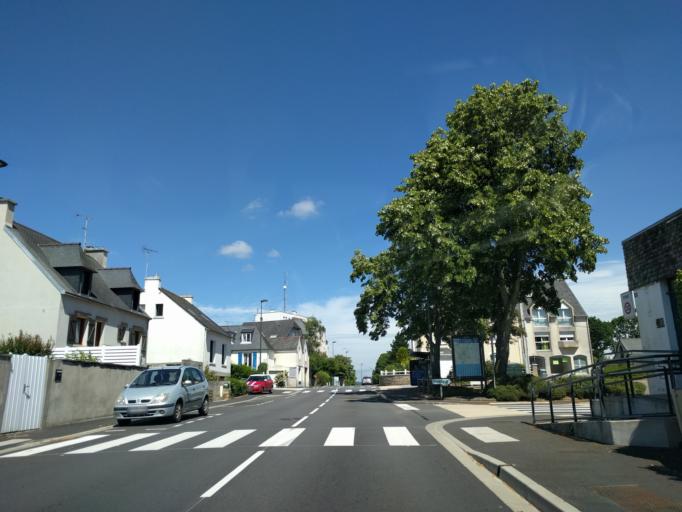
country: FR
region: Brittany
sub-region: Departement du Finistere
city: Quimper
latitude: 47.9887
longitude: -4.0991
